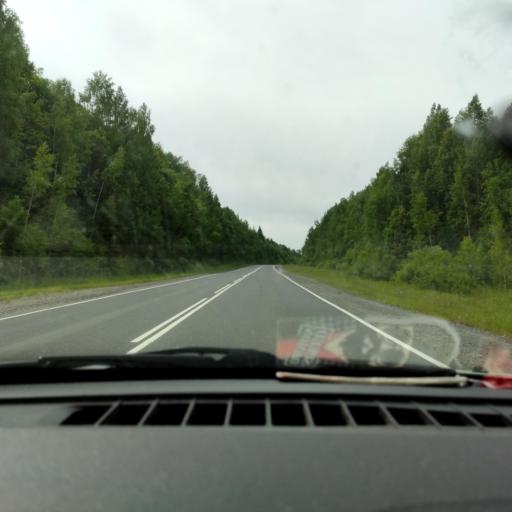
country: RU
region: Perm
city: Pashiya
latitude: 58.3709
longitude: 58.0339
